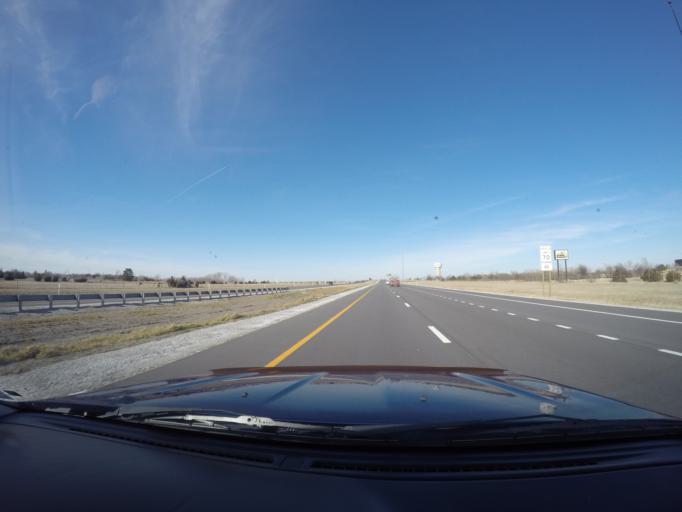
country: US
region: Kansas
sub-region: Sedgwick County
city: Park City
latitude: 37.8328
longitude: -97.3269
